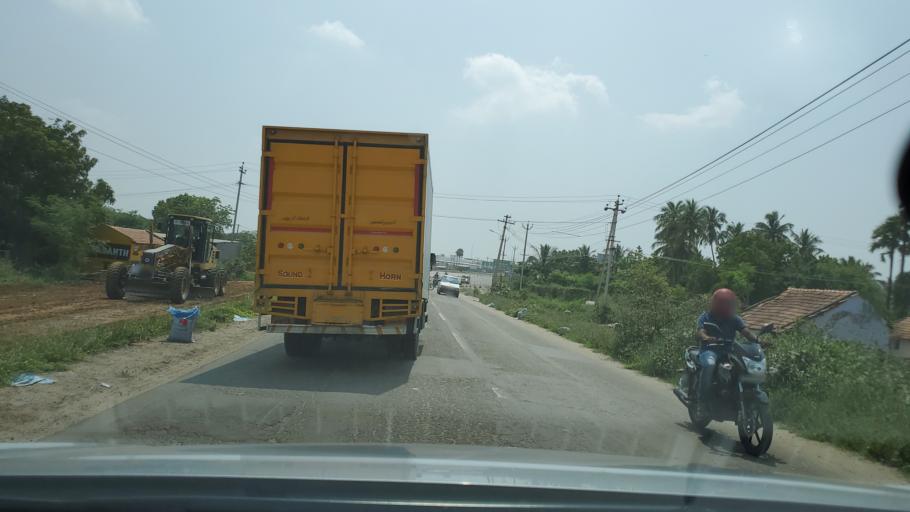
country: IN
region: Tamil Nadu
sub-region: Tiruppur
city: Dharapuram
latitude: 10.7447
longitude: 77.5189
